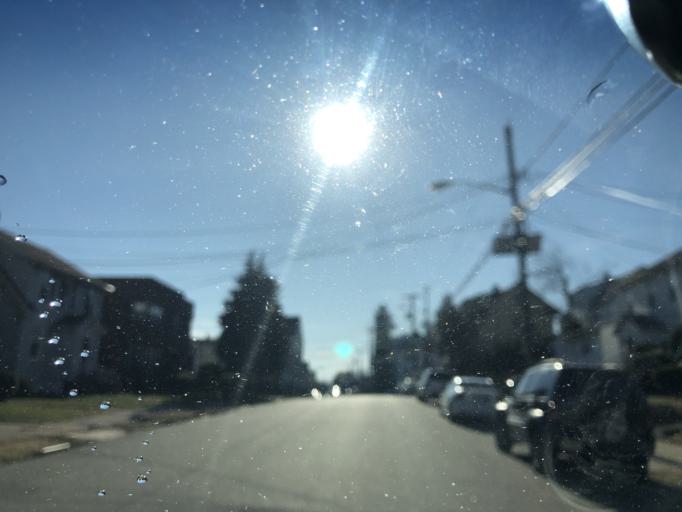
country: US
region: New Jersey
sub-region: Bergen County
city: Fair Lawn
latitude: 40.9225
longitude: -74.1438
